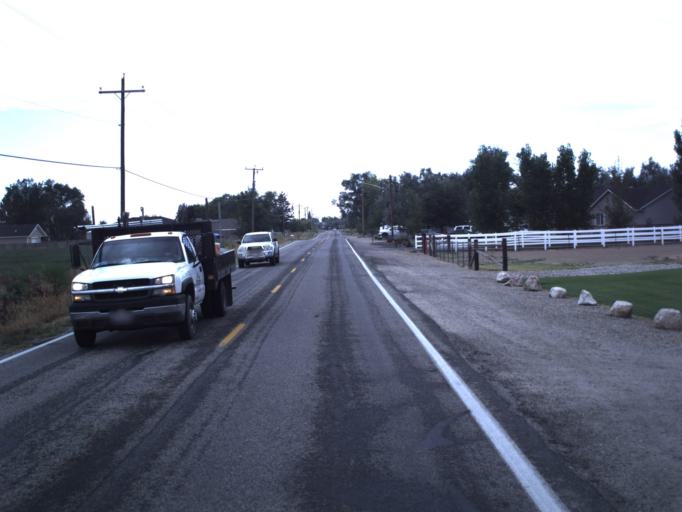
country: US
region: Utah
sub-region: Weber County
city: Hooper
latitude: 41.1339
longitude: -112.1125
